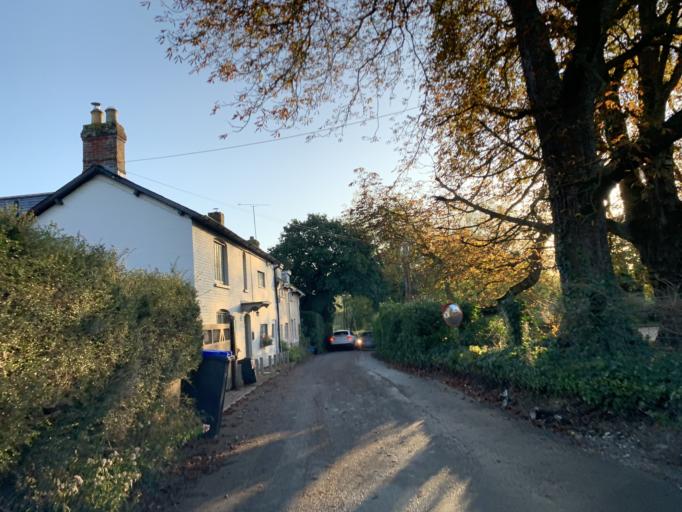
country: GB
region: England
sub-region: Wiltshire
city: Woodford
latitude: 51.1236
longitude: -1.8307
